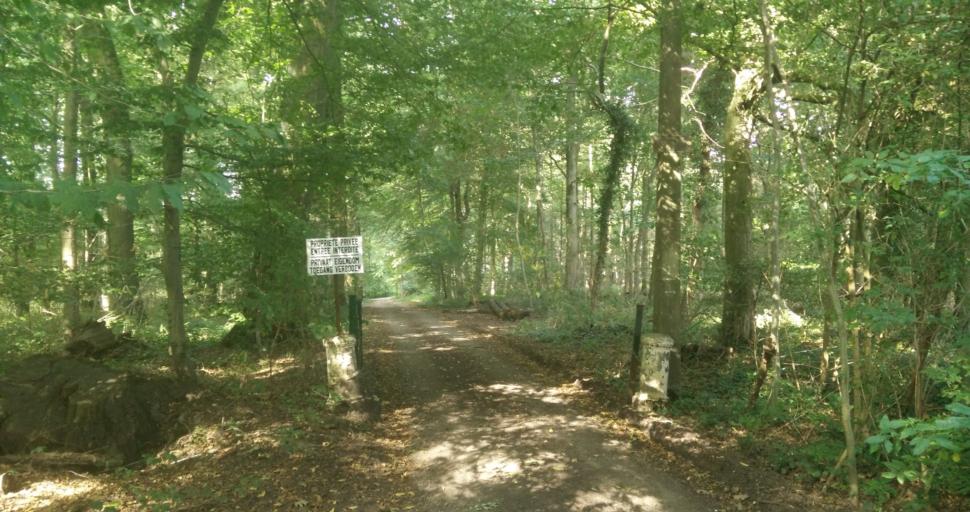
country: BE
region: Wallonia
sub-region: Province du Brabant Wallon
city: Braine-le-Chateau
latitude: 50.6920
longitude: 4.2483
